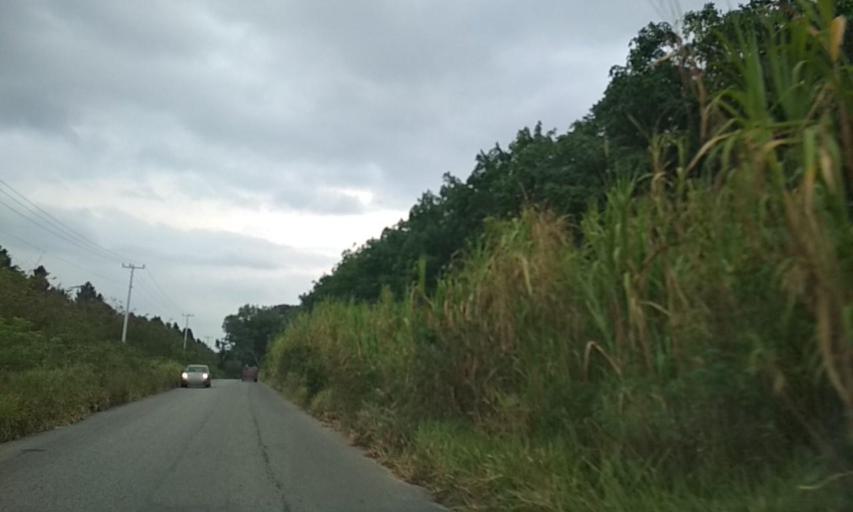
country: MX
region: Veracruz
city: Las Choapas
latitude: 17.8105
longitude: -94.1082
